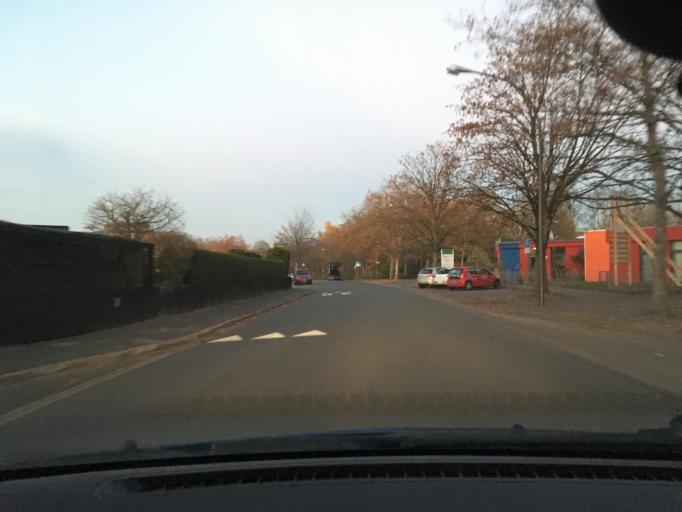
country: DE
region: Lower Saxony
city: Uelzen
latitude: 52.9561
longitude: 10.5594
